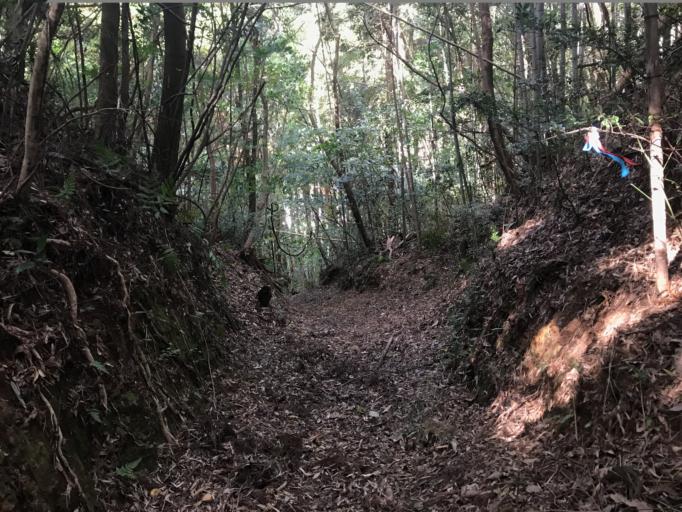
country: JP
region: Saga Prefecture
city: Takeocho-takeo
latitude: 33.1849
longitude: 130.0339
